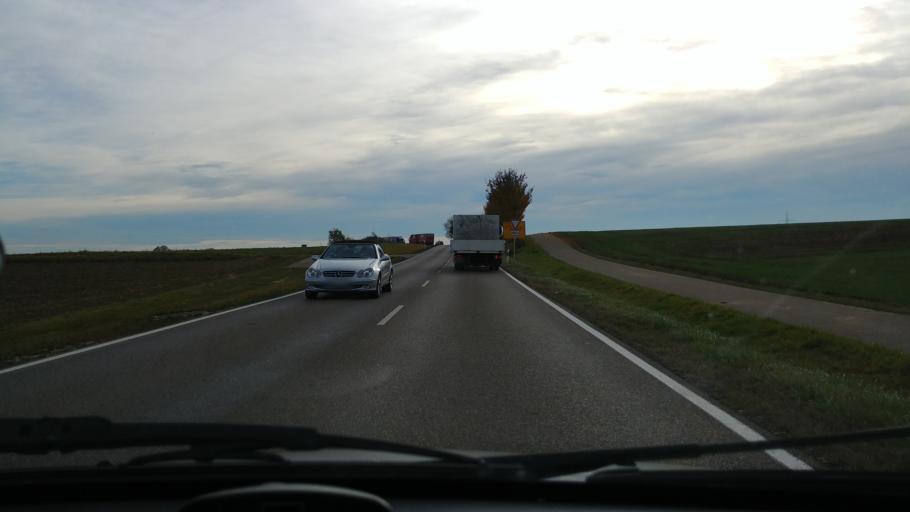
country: DE
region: Bavaria
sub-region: Swabia
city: Bachhagel
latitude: 48.6330
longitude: 10.2949
